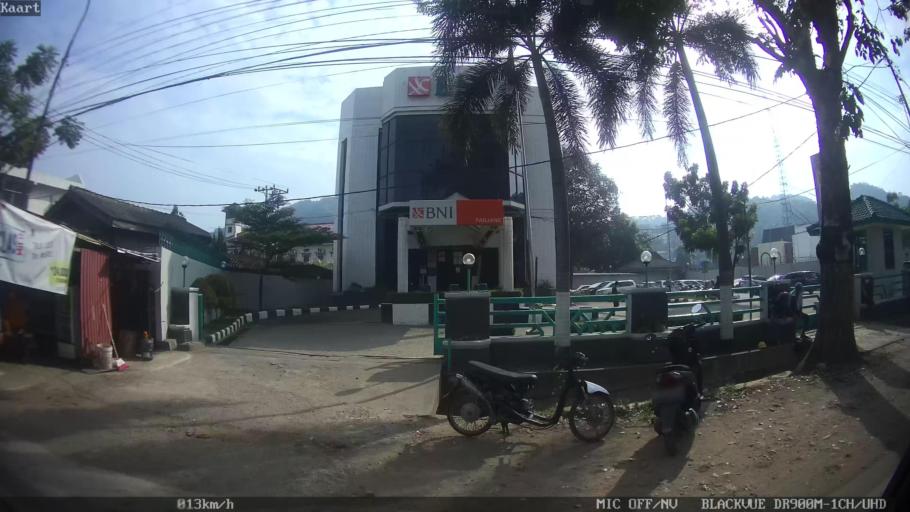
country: ID
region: Lampung
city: Panjang
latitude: -5.4656
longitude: 105.3195
